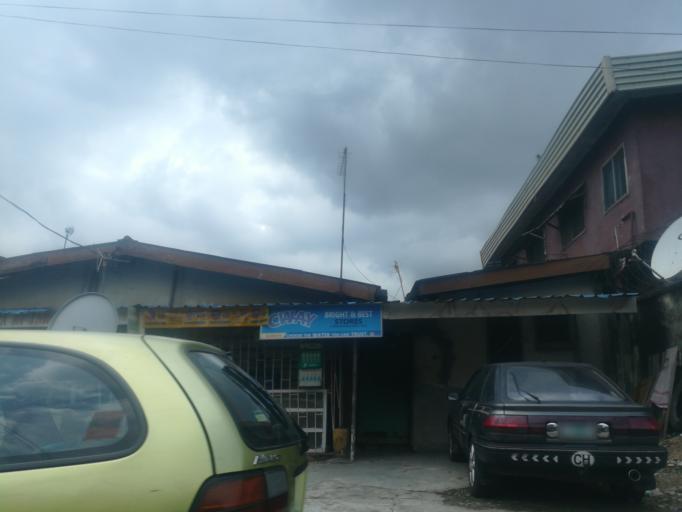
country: NG
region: Lagos
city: Ojota
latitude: 6.5957
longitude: 3.3874
